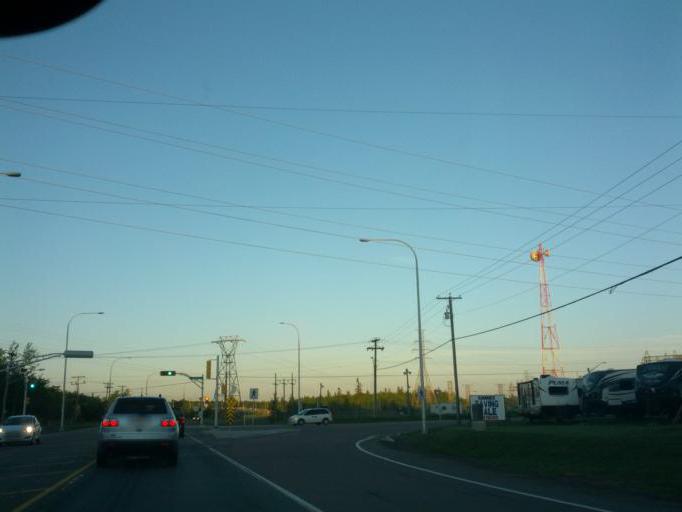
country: CA
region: New Brunswick
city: Moncton
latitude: 46.0960
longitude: -64.8472
